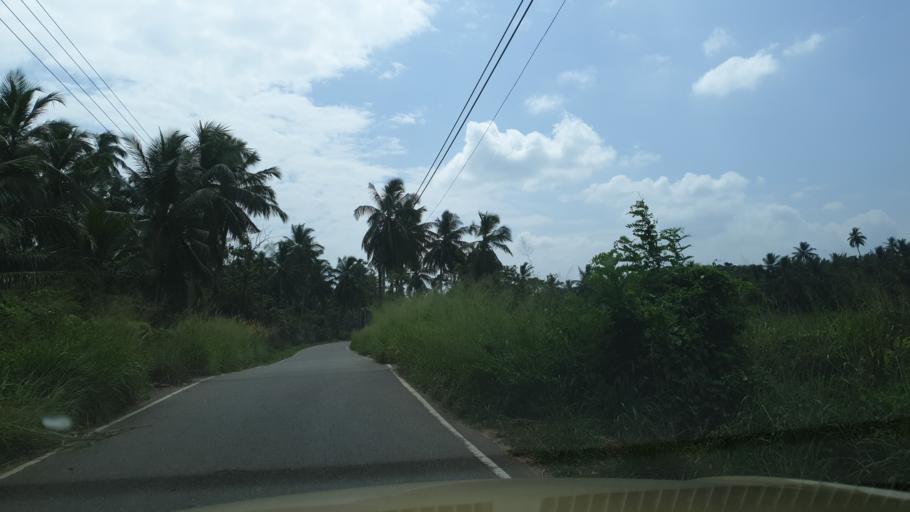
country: LK
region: North Western
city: Kuliyapitiya
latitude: 7.3586
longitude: 79.9675
